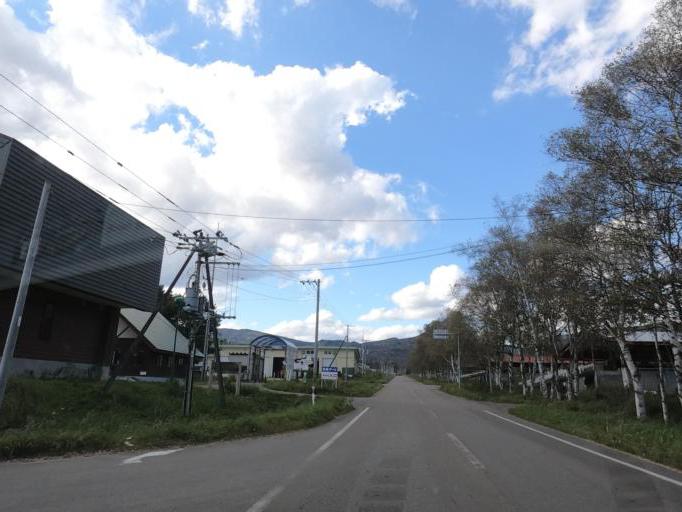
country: JP
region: Hokkaido
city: Otofuke
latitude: 43.2839
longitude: 143.2372
